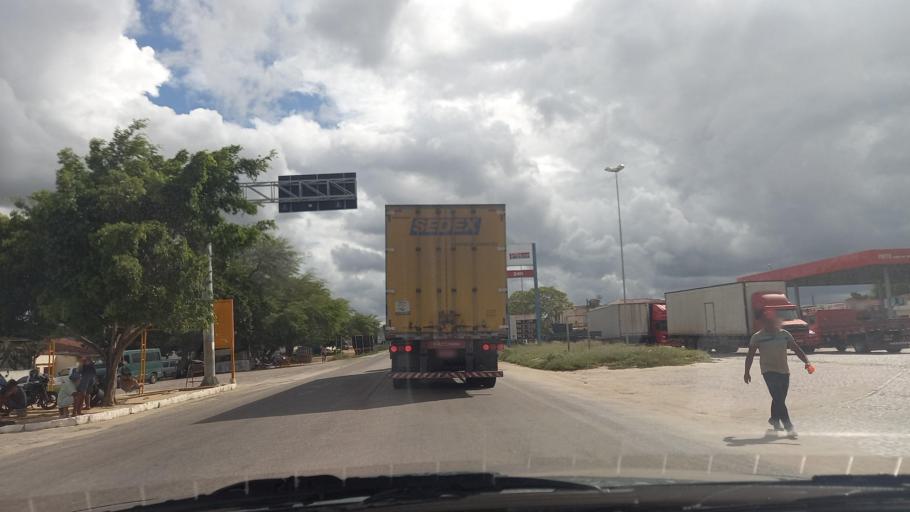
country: BR
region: Pernambuco
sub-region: Lajedo
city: Lajedo
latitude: -8.6590
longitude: -36.3325
